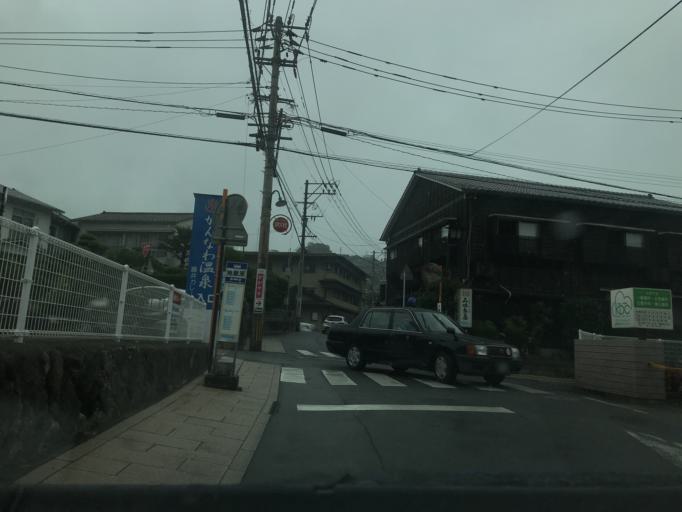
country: JP
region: Oita
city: Beppu
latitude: 33.3154
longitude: 131.4795
